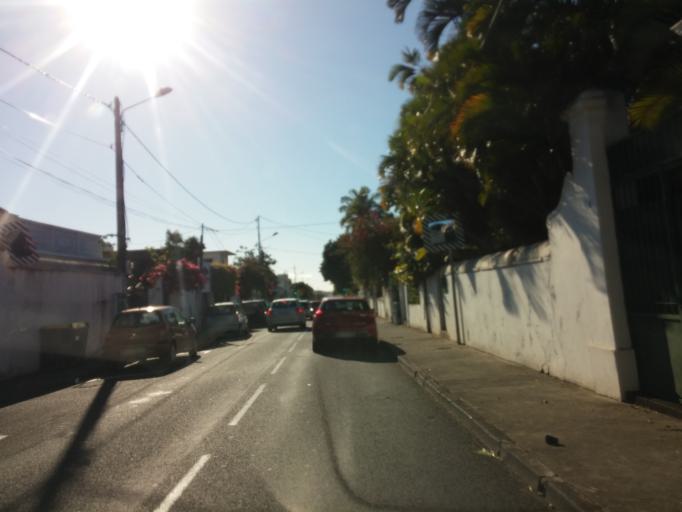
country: RE
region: Reunion
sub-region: Reunion
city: Saint-Denis
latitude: -20.8829
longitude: 55.4504
